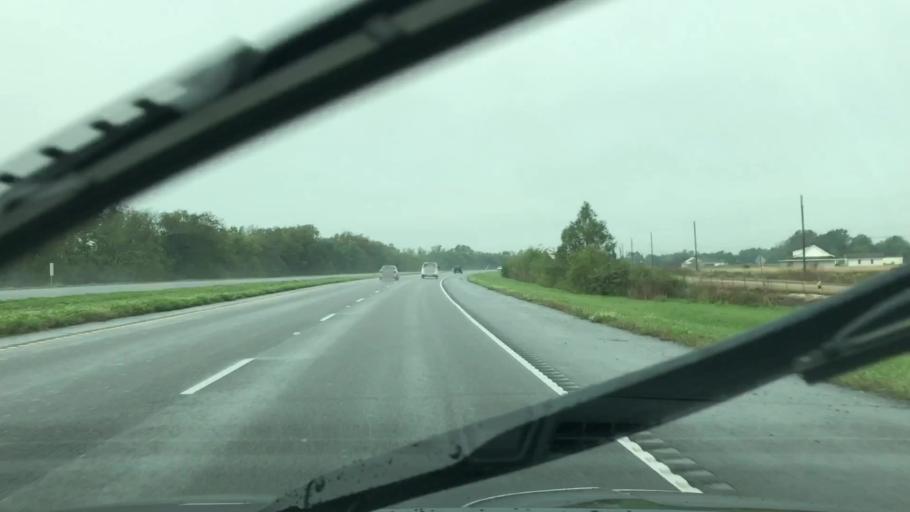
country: US
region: Louisiana
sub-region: Lafourche Parish
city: Raceland
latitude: 29.6919
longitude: -90.5895
